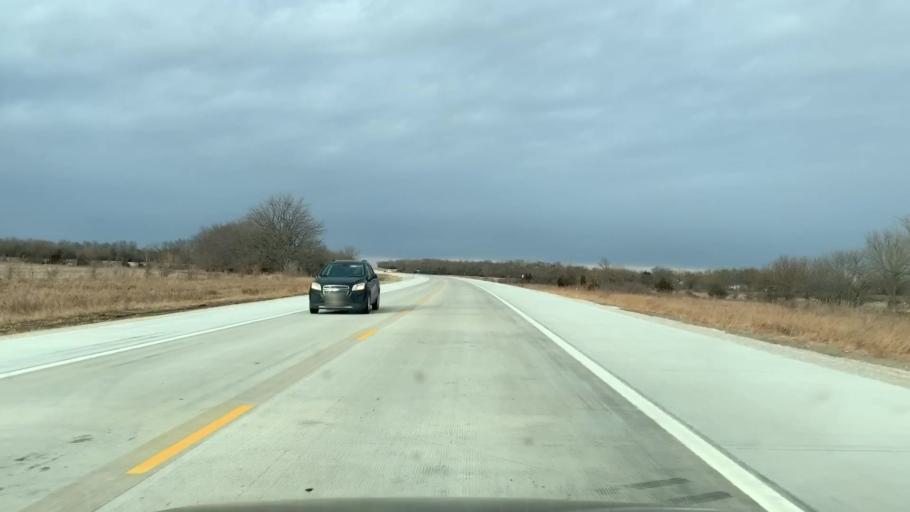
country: US
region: Kansas
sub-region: Allen County
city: Humboldt
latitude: 37.8608
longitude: -95.4051
